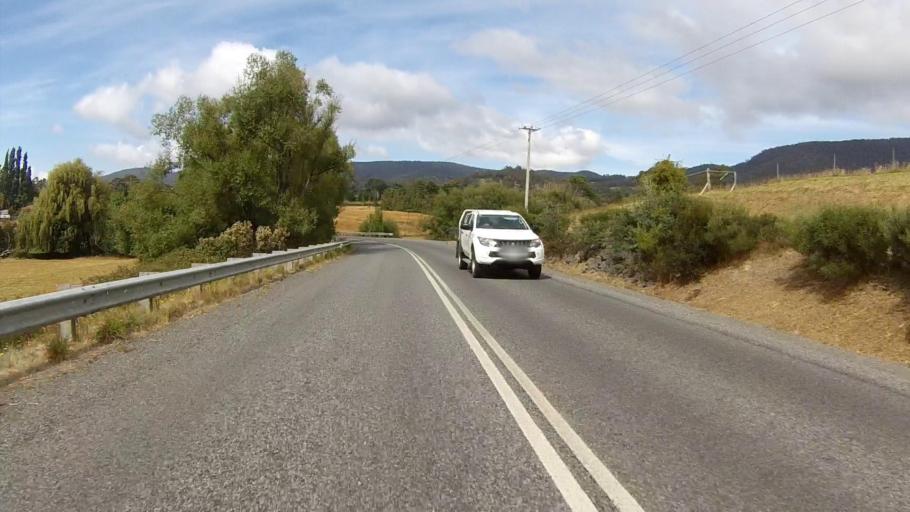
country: AU
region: Tasmania
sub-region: Kingborough
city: Kettering
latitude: -43.1534
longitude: 147.2383
